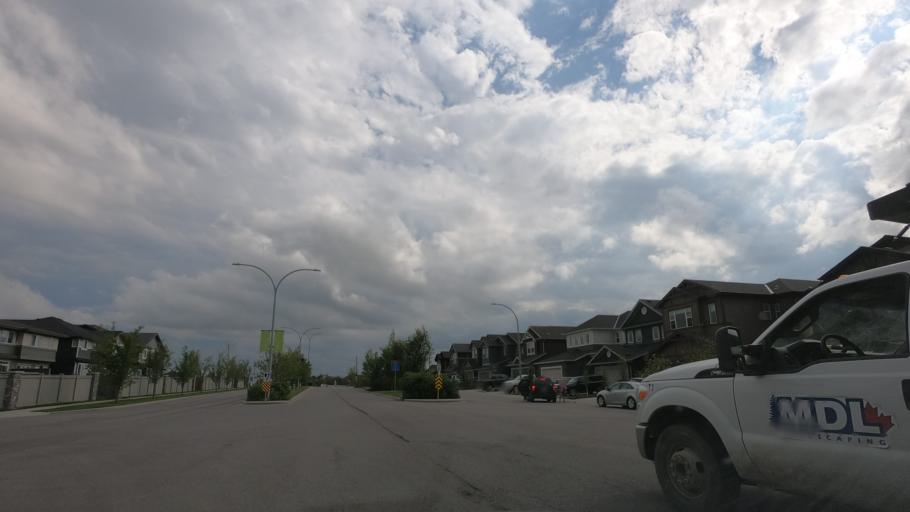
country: CA
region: Alberta
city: Airdrie
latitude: 51.2577
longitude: -113.9919
